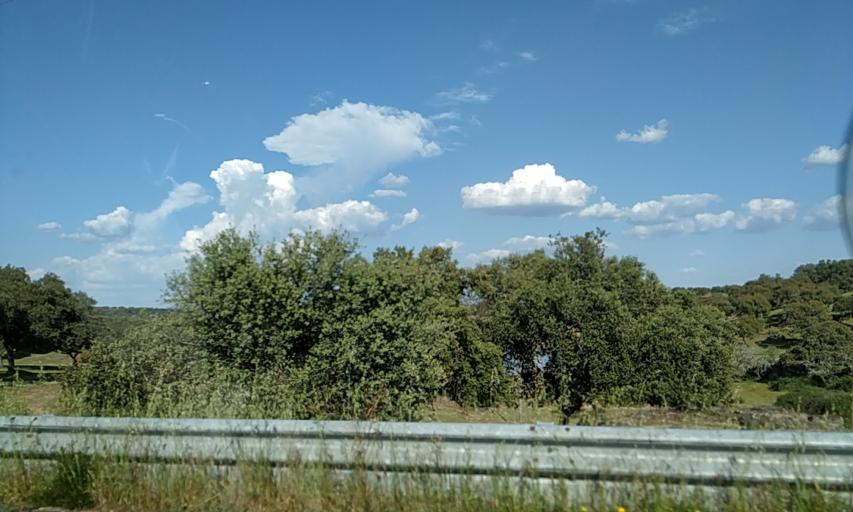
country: PT
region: Evora
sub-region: Estremoz
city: Estremoz
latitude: 38.9904
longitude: -7.4752
